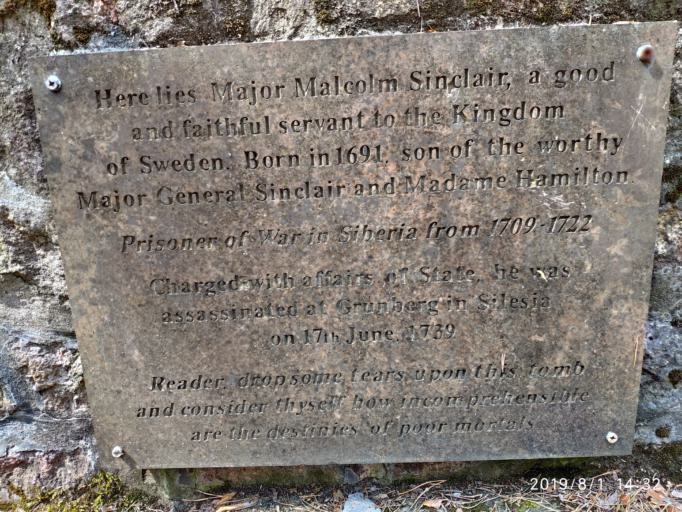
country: PL
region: Lubusz
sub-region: Powiat zielonogorski
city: Nowogrod Bobrzanski
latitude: 51.8113
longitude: 15.2696
